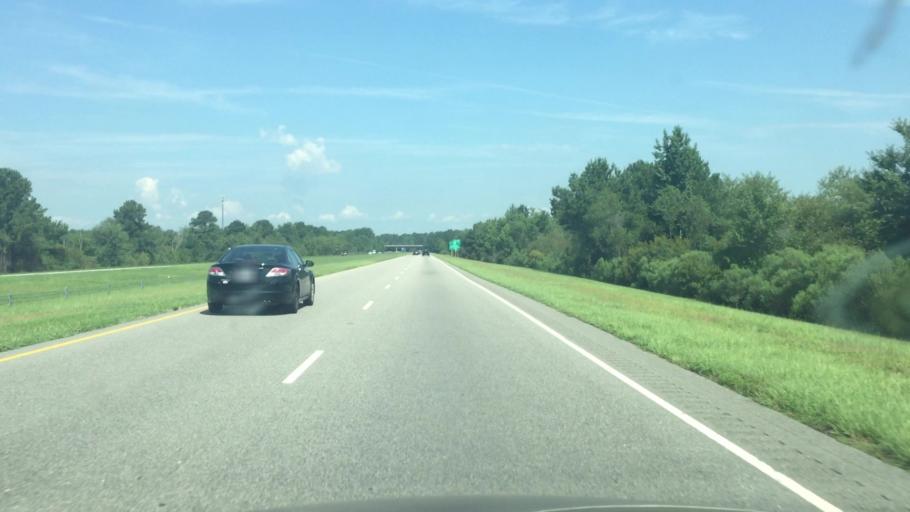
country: US
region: North Carolina
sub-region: Robeson County
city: Maxton
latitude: 34.7382
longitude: -79.3273
